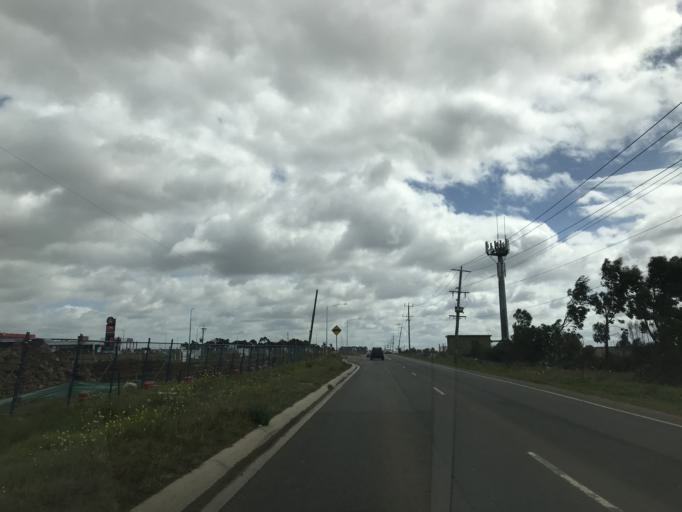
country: AU
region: Victoria
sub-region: Wyndham
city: Truganina
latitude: -37.8332
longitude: 144.7478
